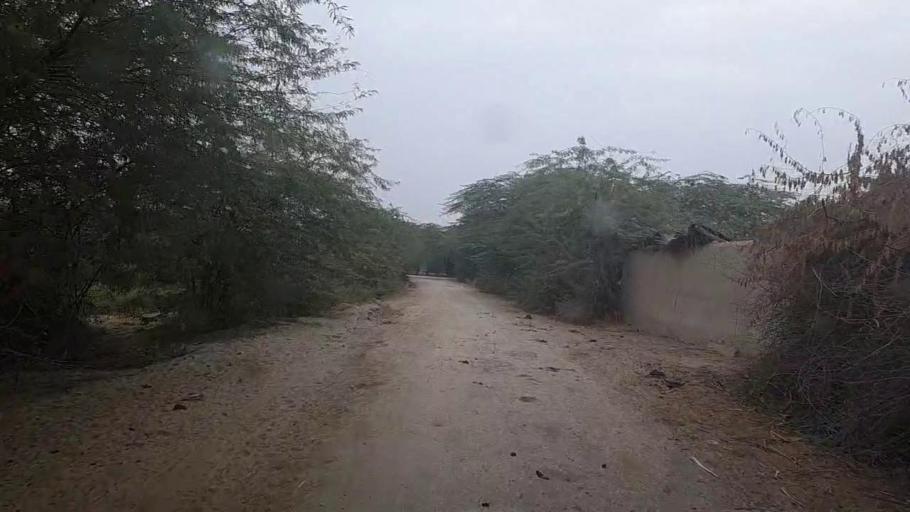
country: PK
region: Sindh
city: Gambat
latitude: 27.3477
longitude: 68.6020
